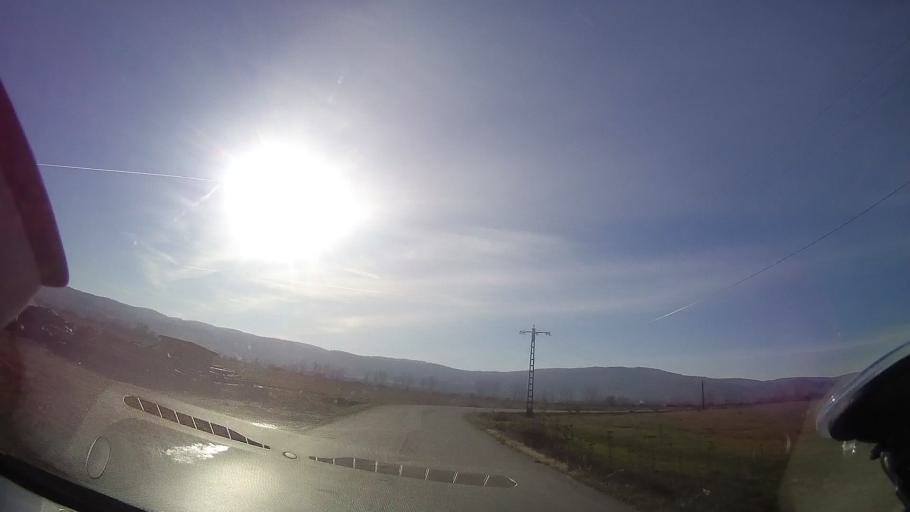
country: RO
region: Bihor
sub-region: Comuna Magesti
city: Magesti
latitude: 47.0171
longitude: 22.4651
